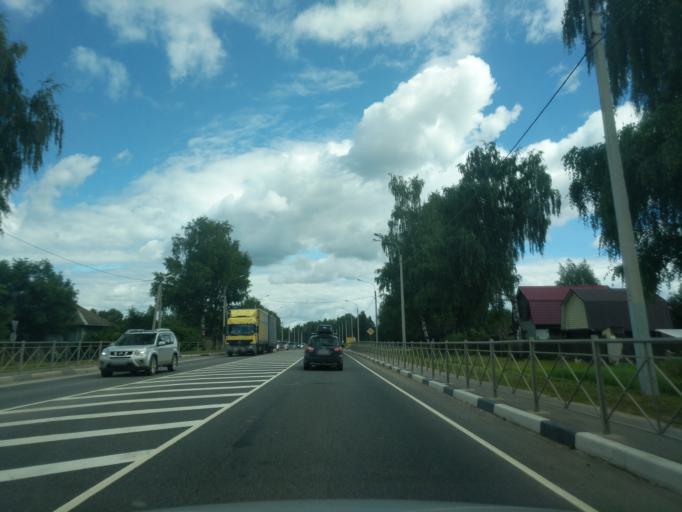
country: RU
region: Jaroslavl
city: Levashevo
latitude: 57.6451
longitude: 40.5373
